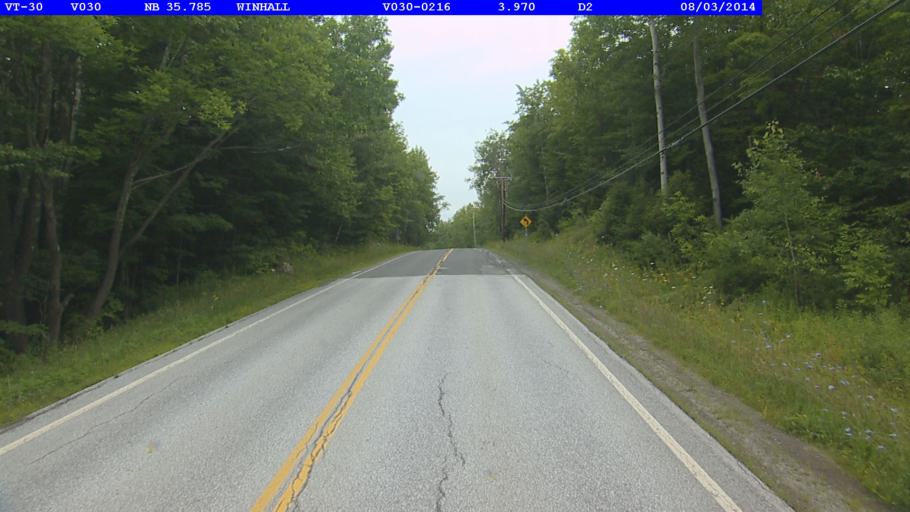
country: US
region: Vermont
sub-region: Bennington County
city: Manchester Center
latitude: 43.1679
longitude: -72.9230
